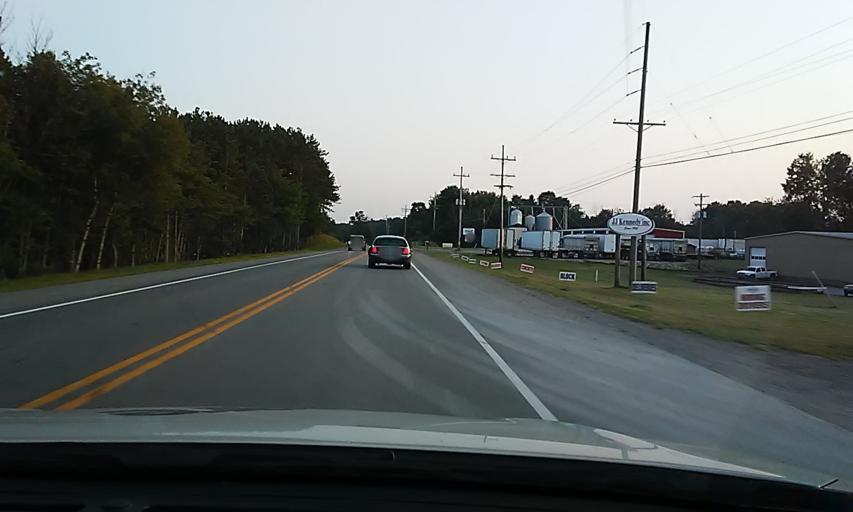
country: US
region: Pennsylvania
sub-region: Clarion County
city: Marianne
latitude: 41.2239
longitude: -79.4342
